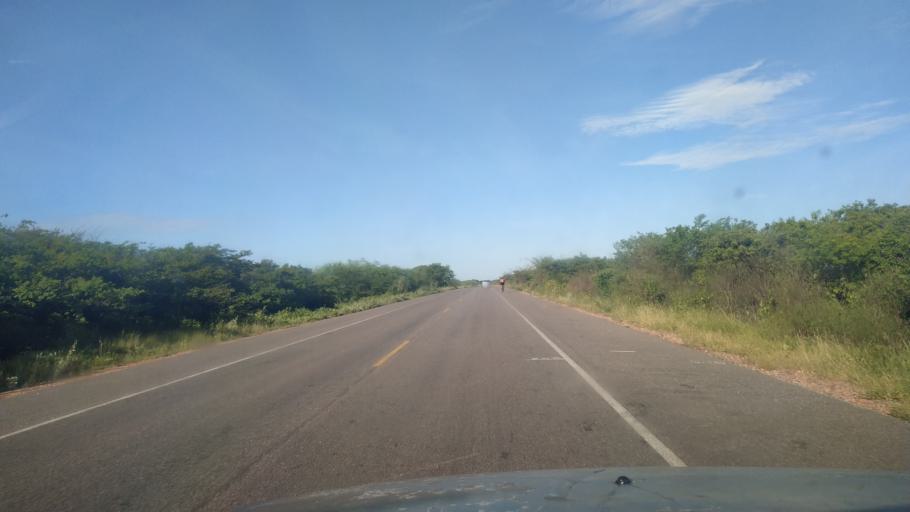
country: BR
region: Rio Grande do Norte
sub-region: Areia Branca
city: Areia Branca
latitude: -5.0450
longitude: -37.1423
